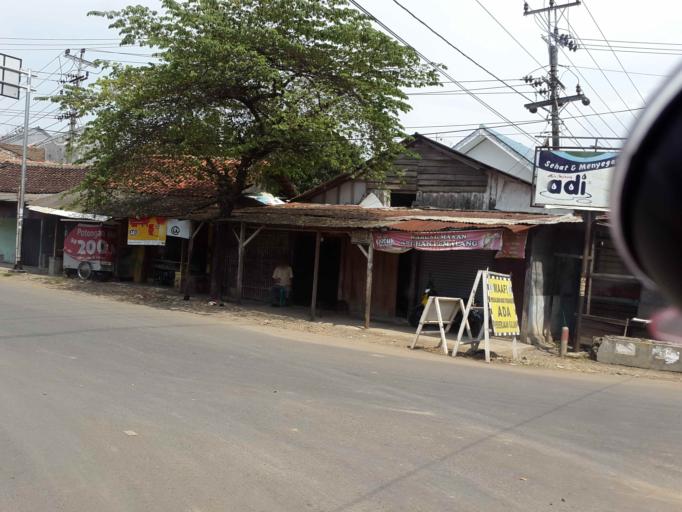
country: ID
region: Central Java
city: Pemalang
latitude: -6.9204
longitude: 109.3844
